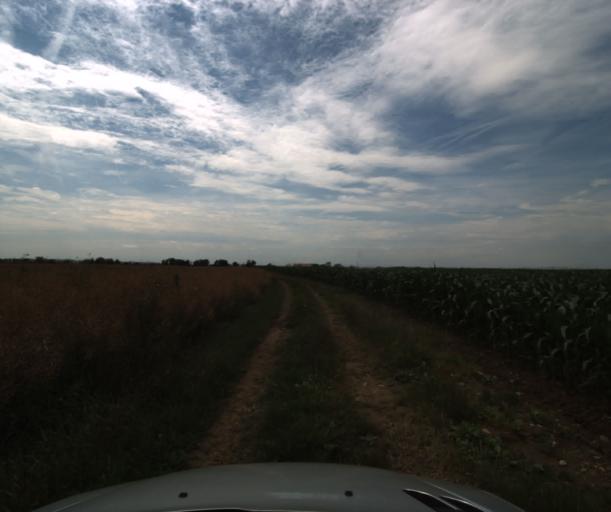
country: FR
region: Midi-Pyrenees
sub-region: Departement de la Haute-Garonne
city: Lacasse
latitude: 43.4169
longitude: 1.2626
